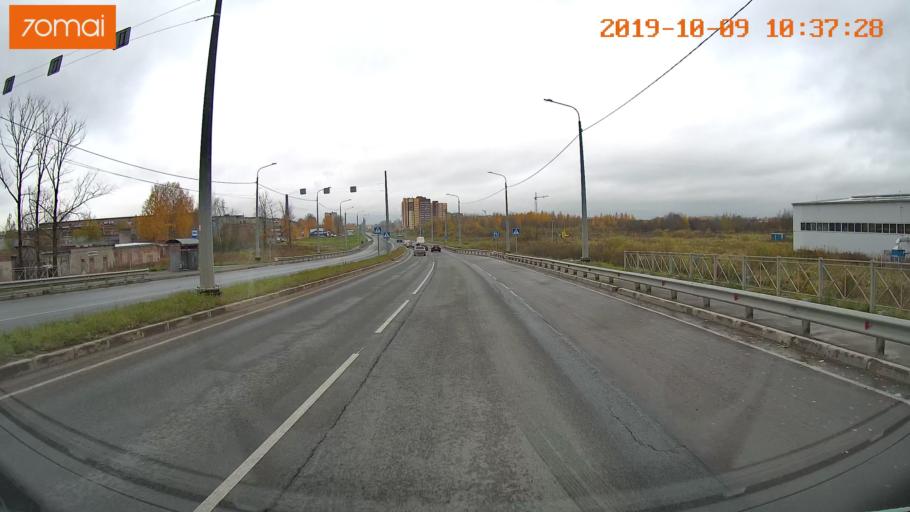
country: RU
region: Vologda
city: Vologda
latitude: 59.2352
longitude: 39.8619
